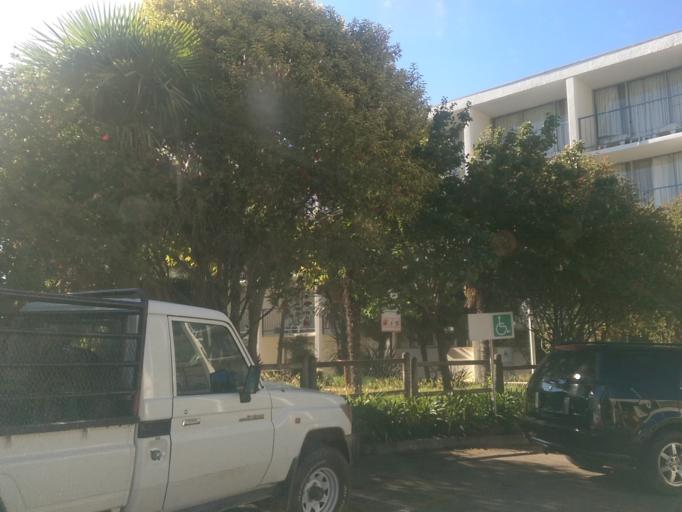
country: LS
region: Maseru
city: Maseru
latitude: -29.3166
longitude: 27.4737
